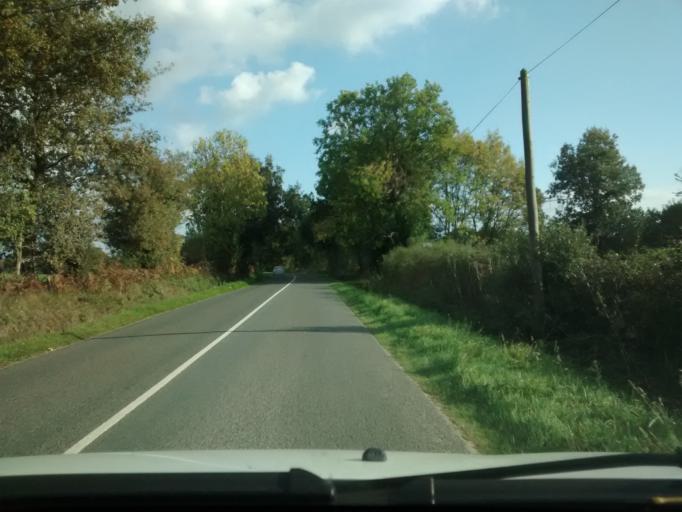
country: FR
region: Pays de la Loire
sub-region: Departement de la Loire-Atlantique
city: Sautron
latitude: 47.2844
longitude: -1.6517
